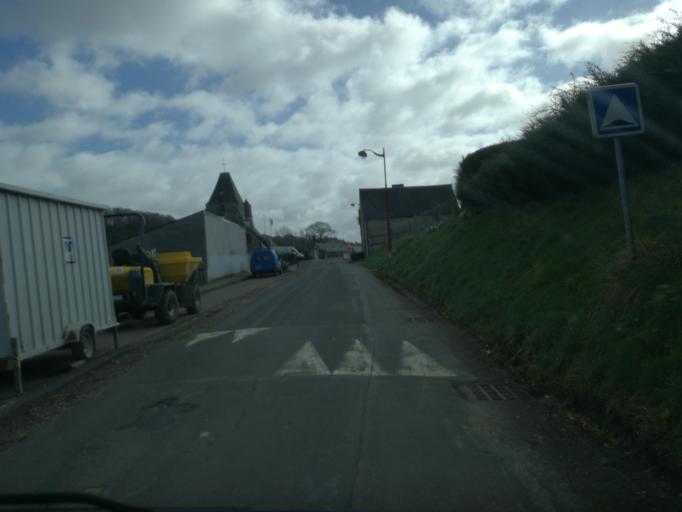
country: FR
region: Haute-Normandie
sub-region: Departement de la Seine-Maritime
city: Bretteville-du-Grand-Caux
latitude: 49.7034
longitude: 0.4478
